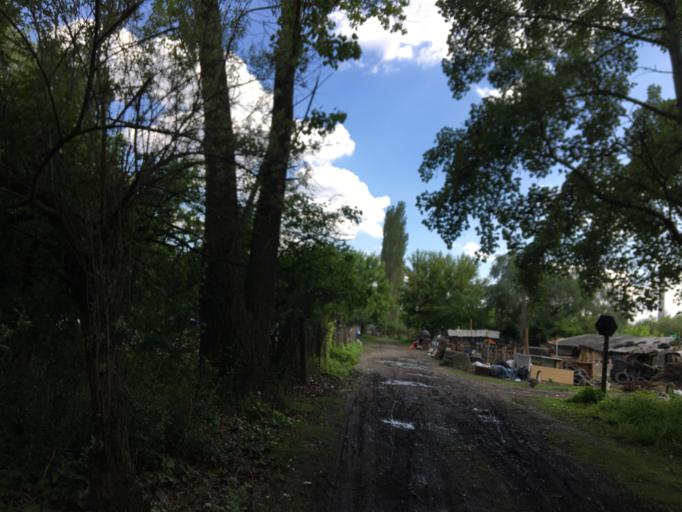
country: HU
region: Pest
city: Urom
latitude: 47.5770
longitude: 19.0388
